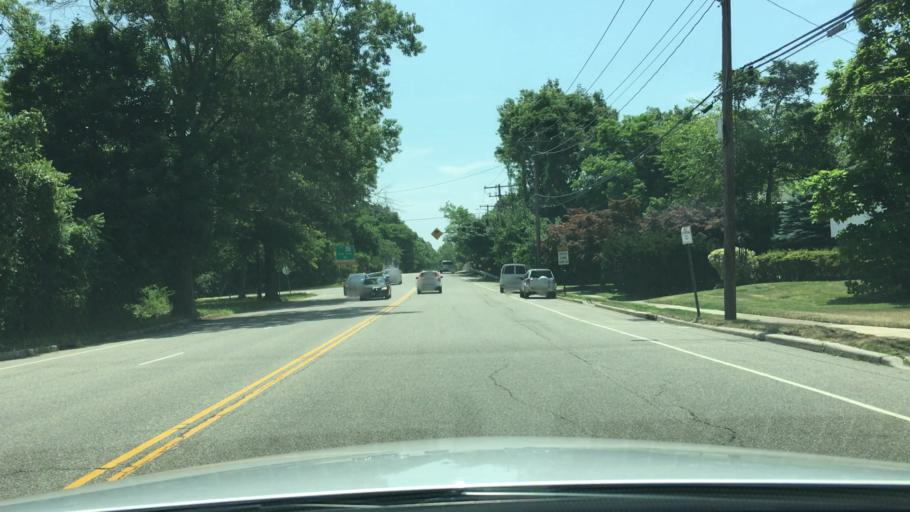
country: US
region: New York
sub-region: Nassau County
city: Plainview
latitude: 40.7969
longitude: -73.4810
